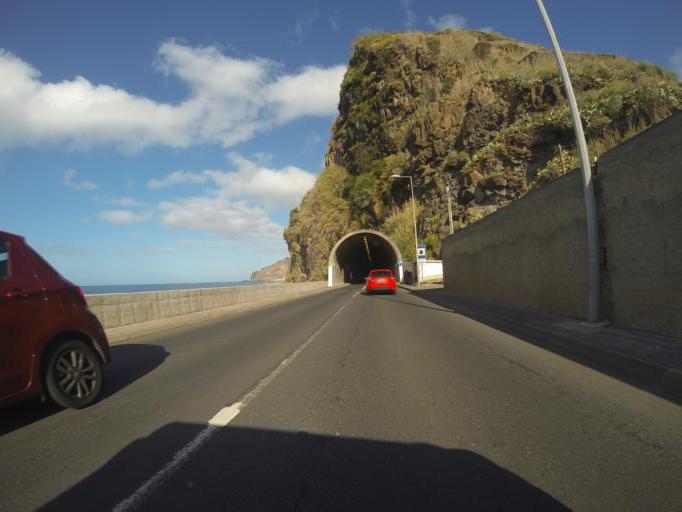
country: PT
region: Madeira
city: Ponta do Sol
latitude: 32.6786
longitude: -17.0818
